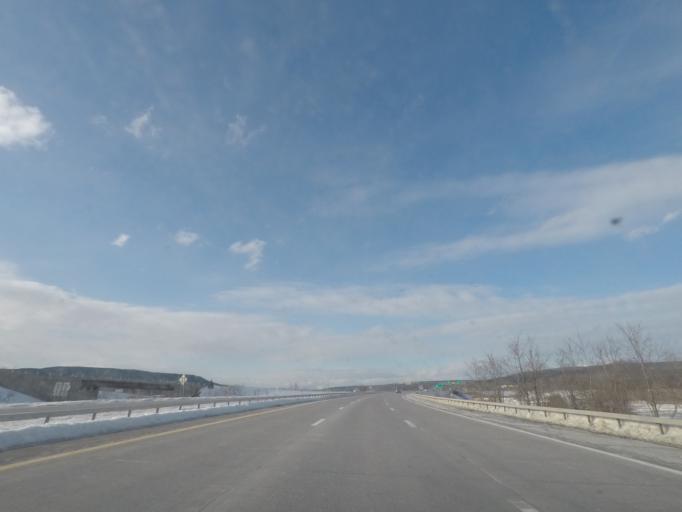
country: US
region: New York
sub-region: Schenectady County
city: Scotia
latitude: 42.8422
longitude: -74.0047
